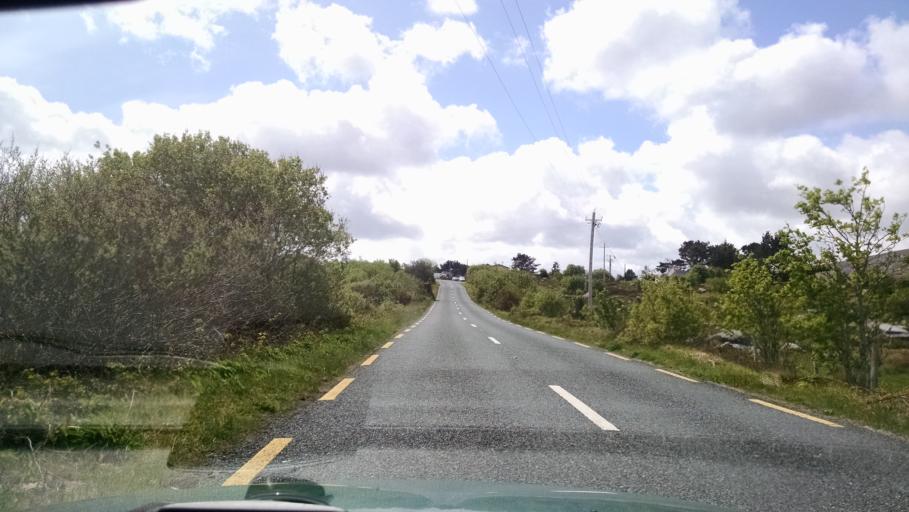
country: IE
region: Connaught
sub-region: County Galway
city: Clifden
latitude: 53.3682
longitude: -9.6872
